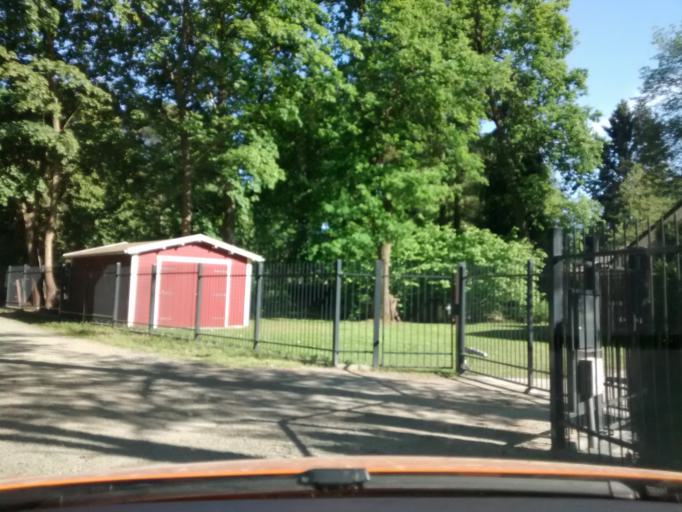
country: DE
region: Brandenburg
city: Bad Saarow
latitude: 52.2626
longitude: 14.0698
